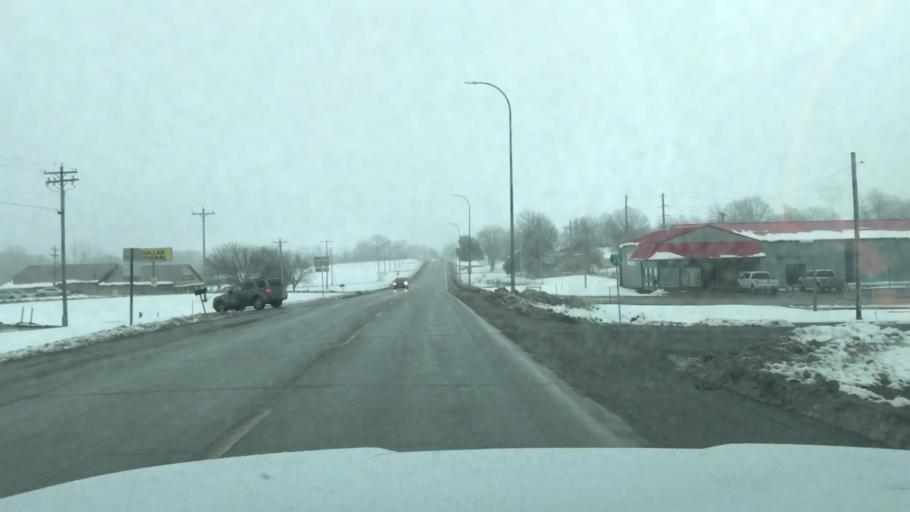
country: US
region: Missouri
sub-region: Clinton County
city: Cameron
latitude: 39.7318
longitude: -94.2355
